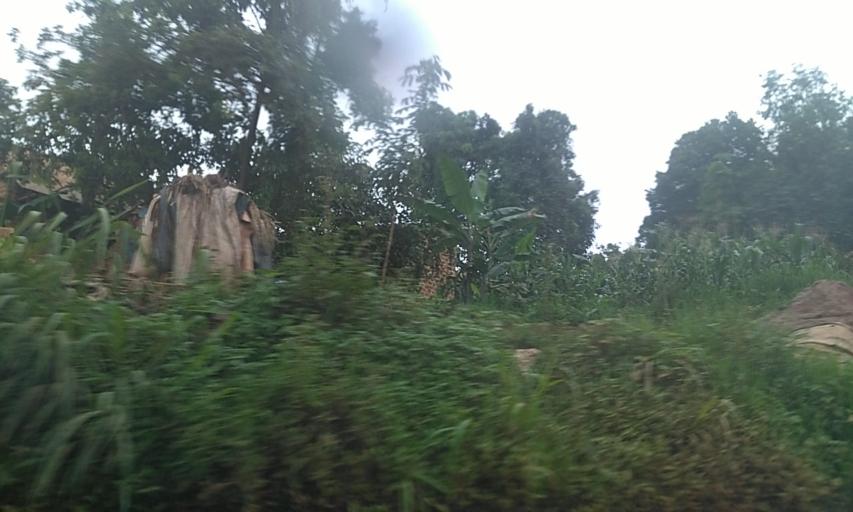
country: UG
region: Central Region
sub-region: Wakiso District
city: Kireka
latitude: 0.4358
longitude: 32.6050
